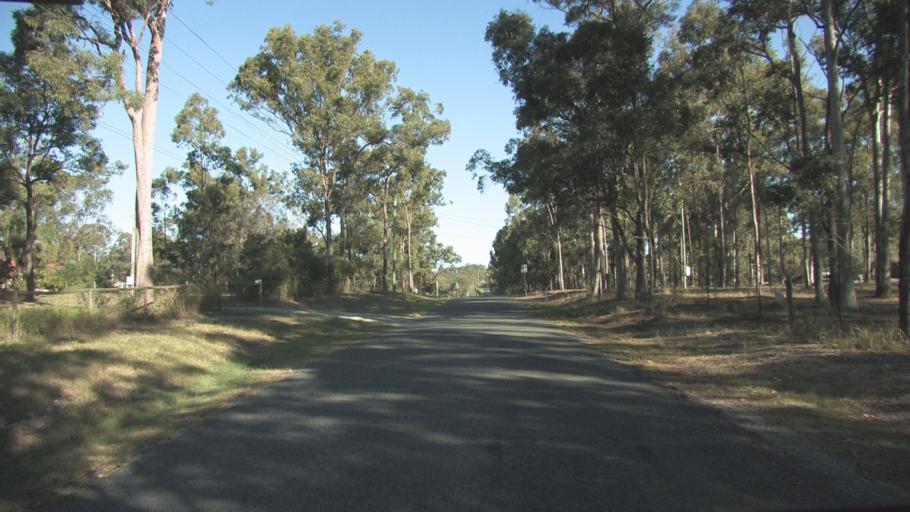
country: AU
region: Queensland
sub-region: Logan
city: Logan Reserve
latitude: -27.7172
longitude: 153.1068
